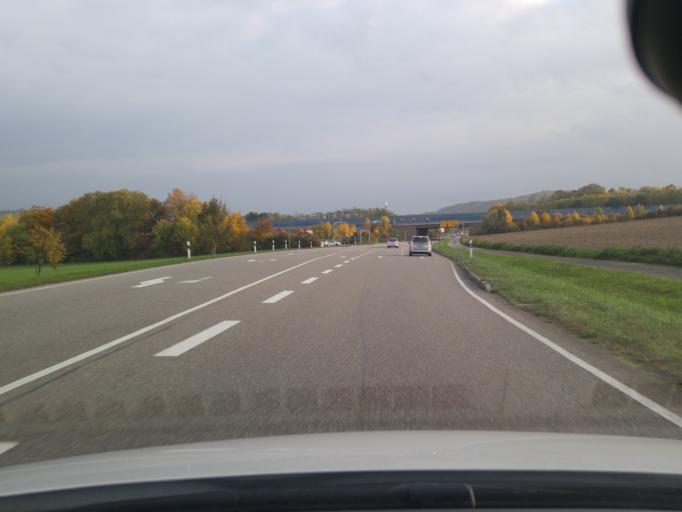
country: DE
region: Baden-Wuerttemberg
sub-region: Karlsruhe Region
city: Rauenberg
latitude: 49.2784
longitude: 8.6926
